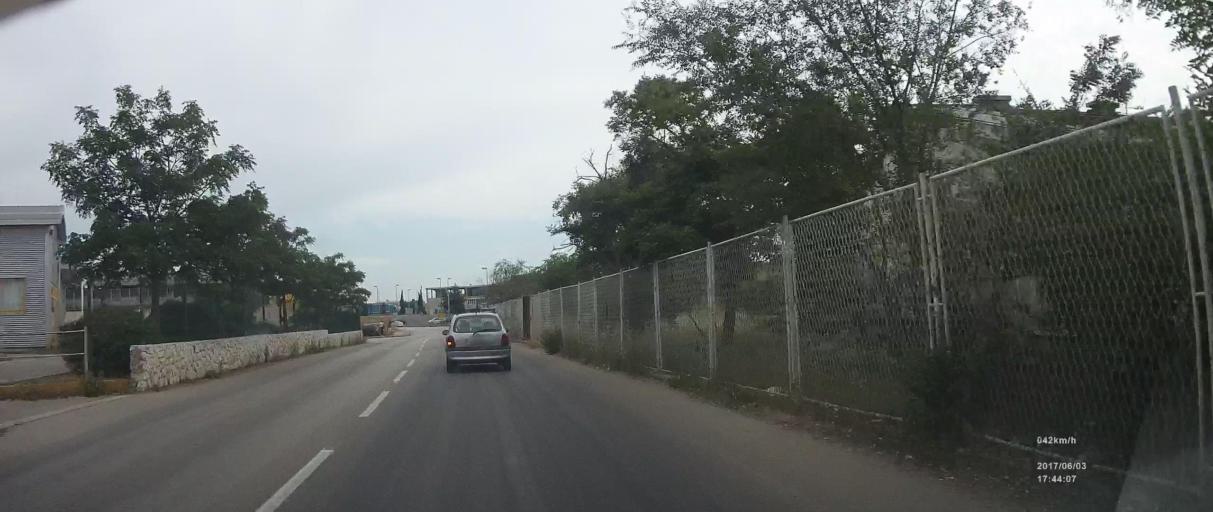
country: HR
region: Sibensko-Kniniska
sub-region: Grad Sibenik
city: Sibenik
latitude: 43.7116
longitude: 15.9101
